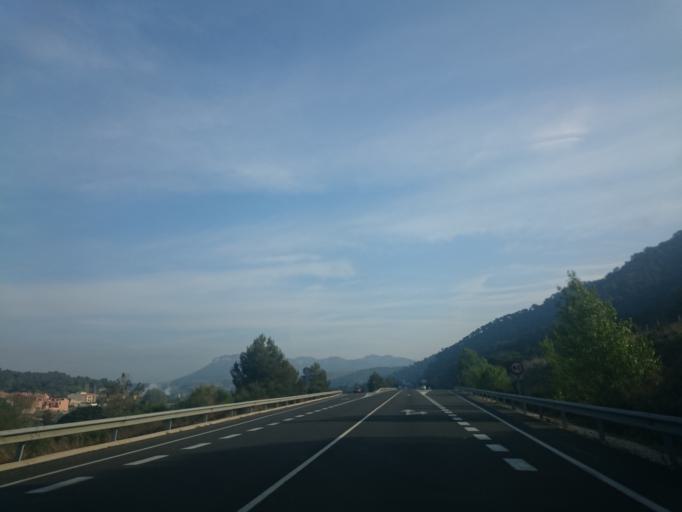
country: ES
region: Catalonia
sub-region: Provincia de Barcelona
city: Capellades
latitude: 41.5393
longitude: 1.6912
